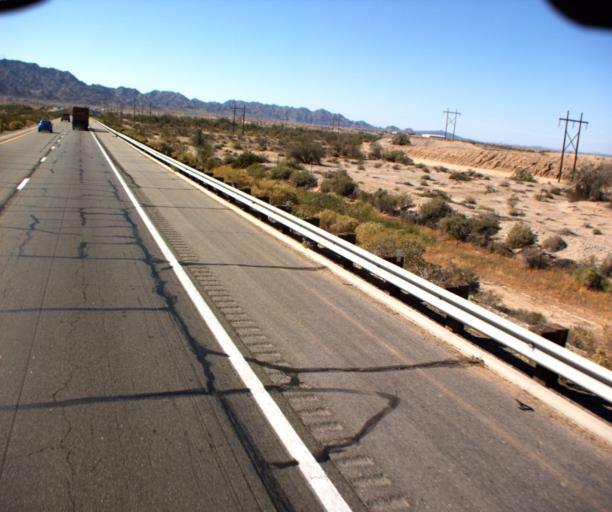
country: US
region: Arizona
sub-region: Yuma County
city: Wellton
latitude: 32.6631
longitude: -114.2669
